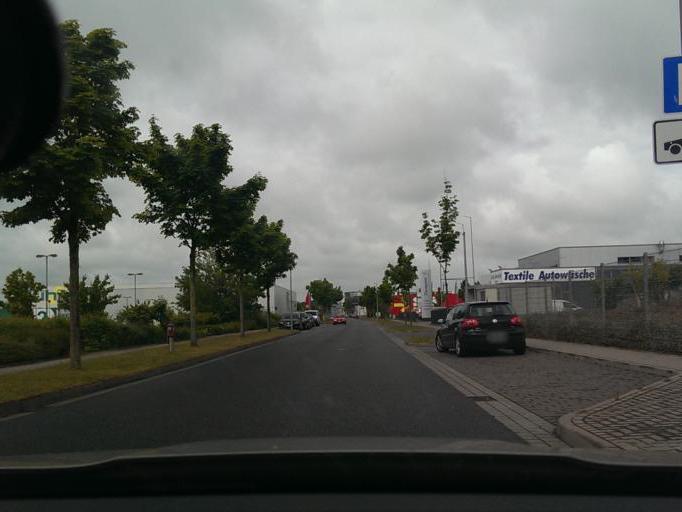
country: DE
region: Lower Saxony
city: Wolfsburg
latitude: 52.3700
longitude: 10.7360
